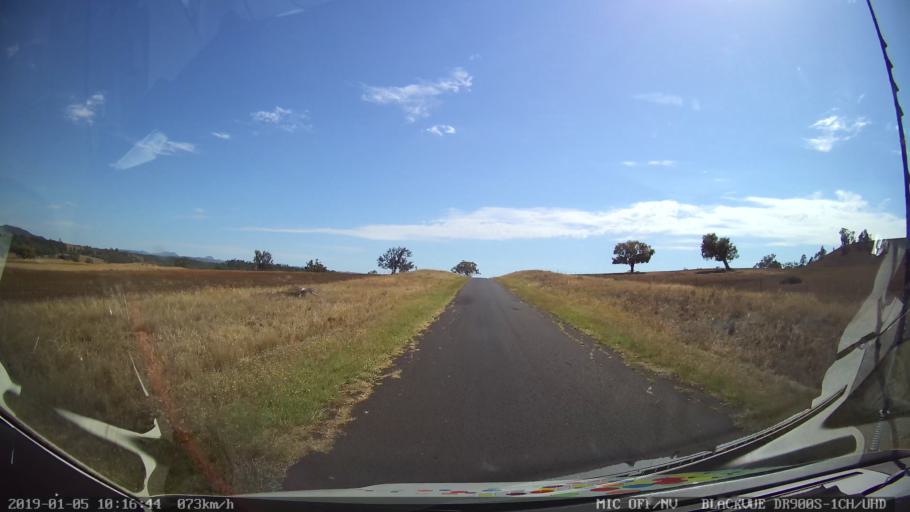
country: AU
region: New South Wales
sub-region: Gilgandra
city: Gilgandra
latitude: -31.5726
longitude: 148.9551
